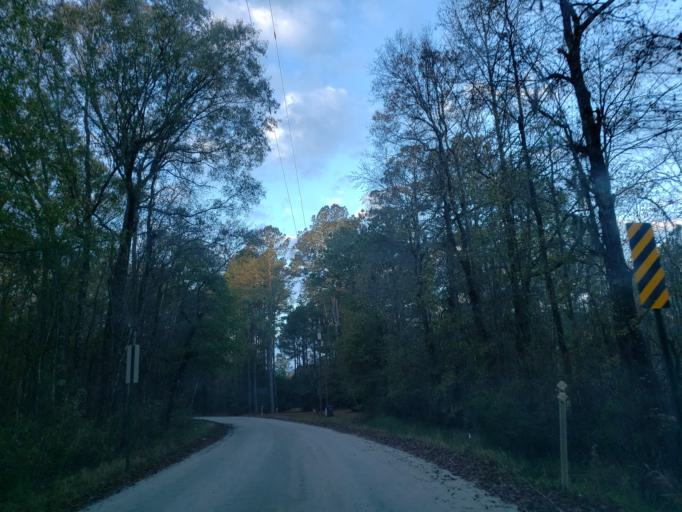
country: US
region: Georgia
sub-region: Chatham County
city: Bloomingdale
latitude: 32.1198
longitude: -81.3359
